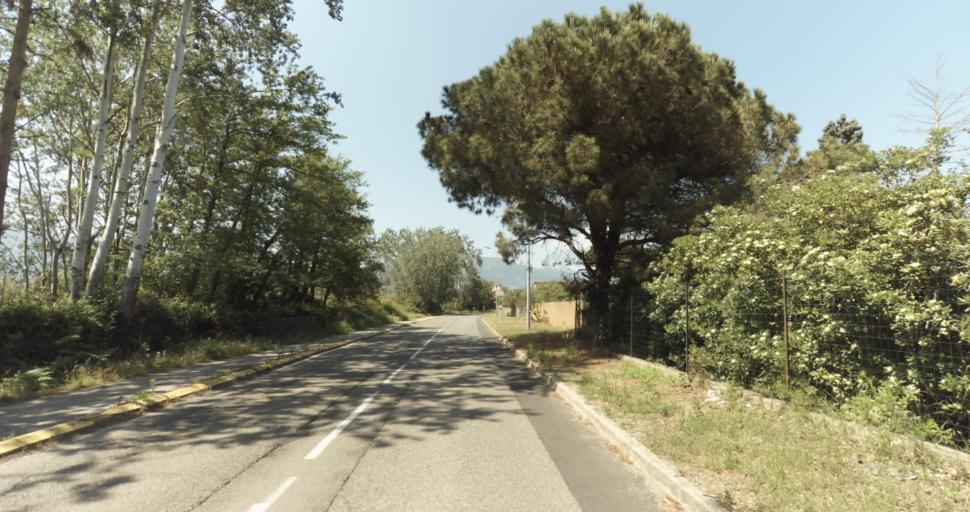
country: FR
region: Corsica
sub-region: Departement de la Haute-Corse
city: Biguglia
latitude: 42.6374
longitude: 9.4604
